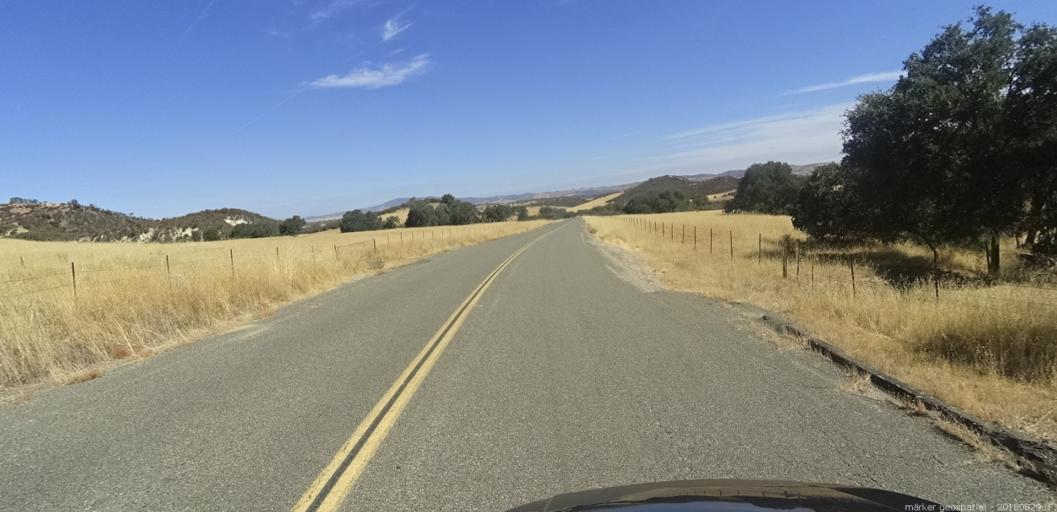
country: US
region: California
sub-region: San Luis Obispo County
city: Lake Nacimiento
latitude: 35.7929
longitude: -120.9742
